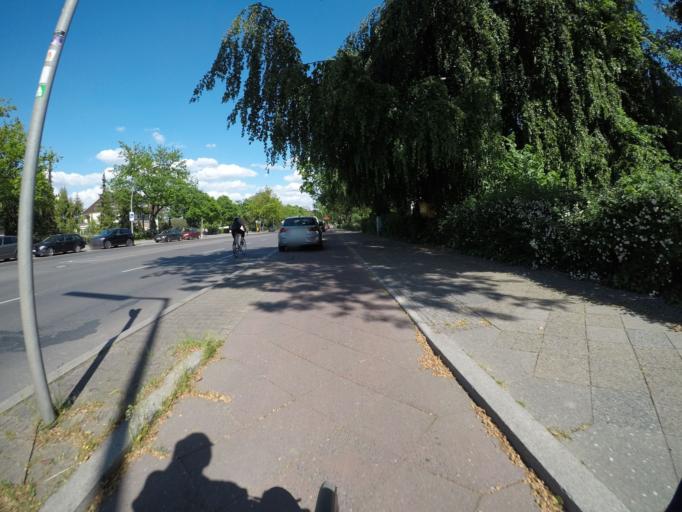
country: DE
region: Berlin
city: Wannsee
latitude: 52.4204
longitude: 13.1674
